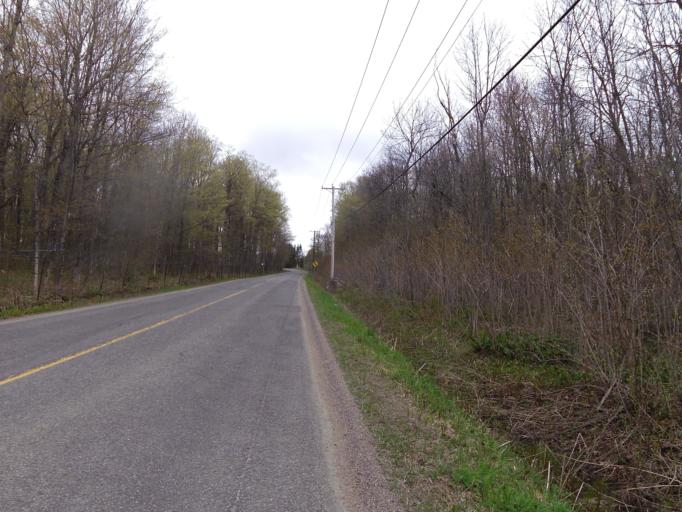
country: CA
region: Quebec
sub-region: Laurentides
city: Brownsburg-Chatham
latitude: 45.6097
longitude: -74.4796
